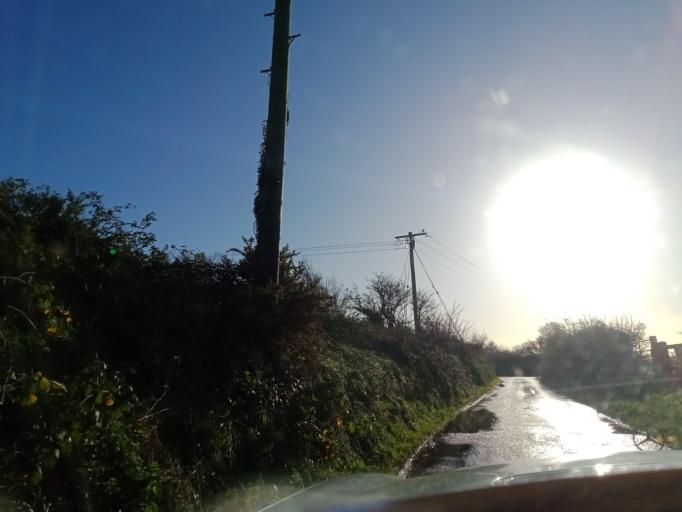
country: IE
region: Leinster
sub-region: Kilkenny
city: Mooncoin
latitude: 52.2866
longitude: -7.1929
